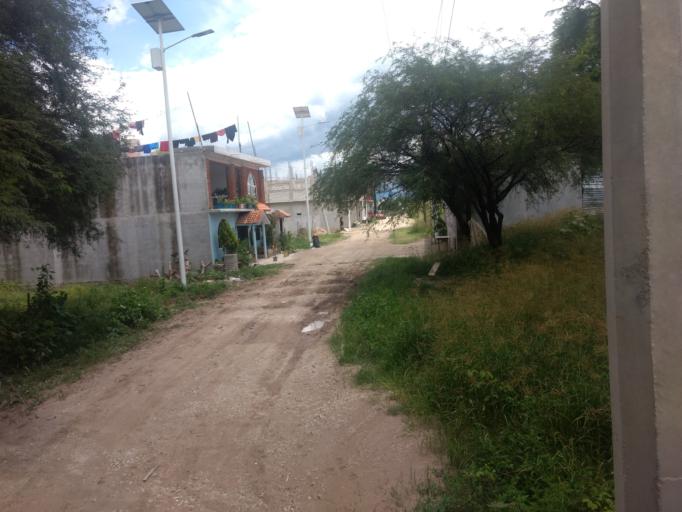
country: MX
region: Oaxaca
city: Ciudad de Huajuapam de Leon
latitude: 17.8156
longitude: -97.7928
